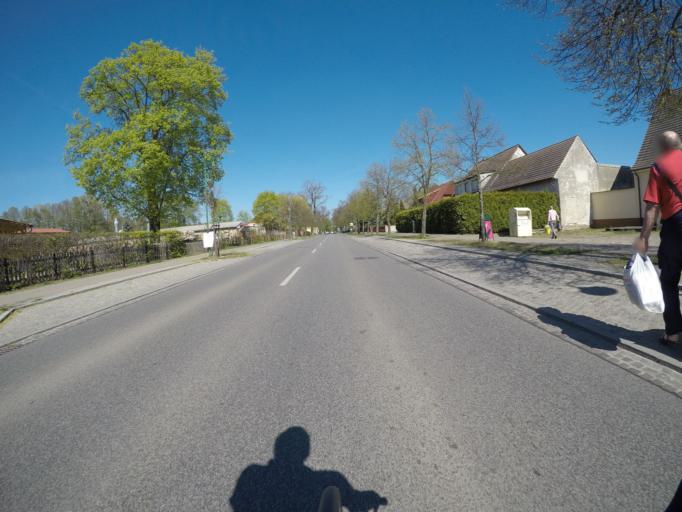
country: DE
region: Brandenburg
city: Werneuchen
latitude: 52.6311
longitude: 13.7387
